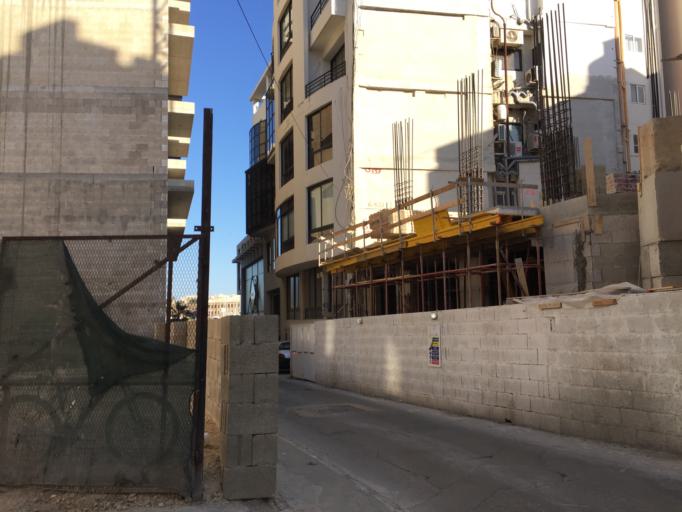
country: MT
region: Tas-Sliema
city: Sliema
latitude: 35.9077
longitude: 14.4979
